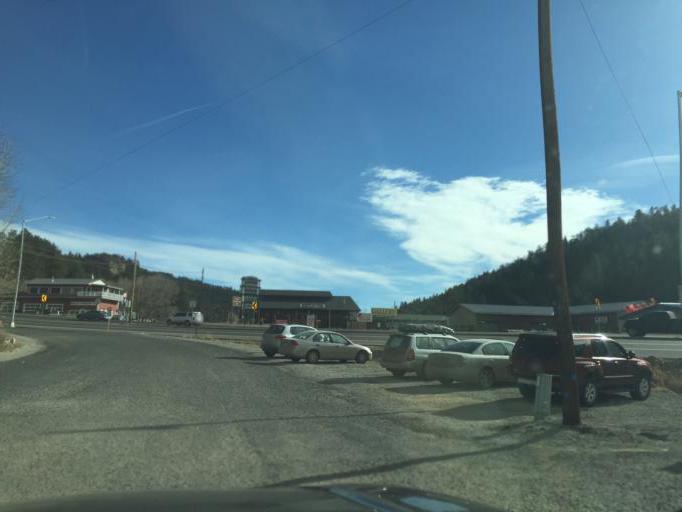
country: US
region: Colorado
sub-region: Jefferson County
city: Evergreen
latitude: 39.4058
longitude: -105.4749
